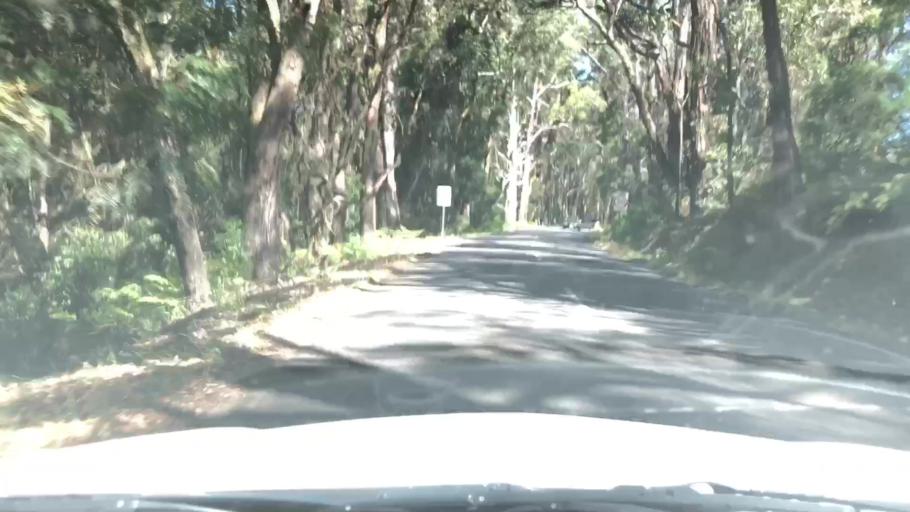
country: AU
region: Victoria
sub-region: Yarra Ranges
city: Macclesfield
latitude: -37.9134
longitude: 145.4695
